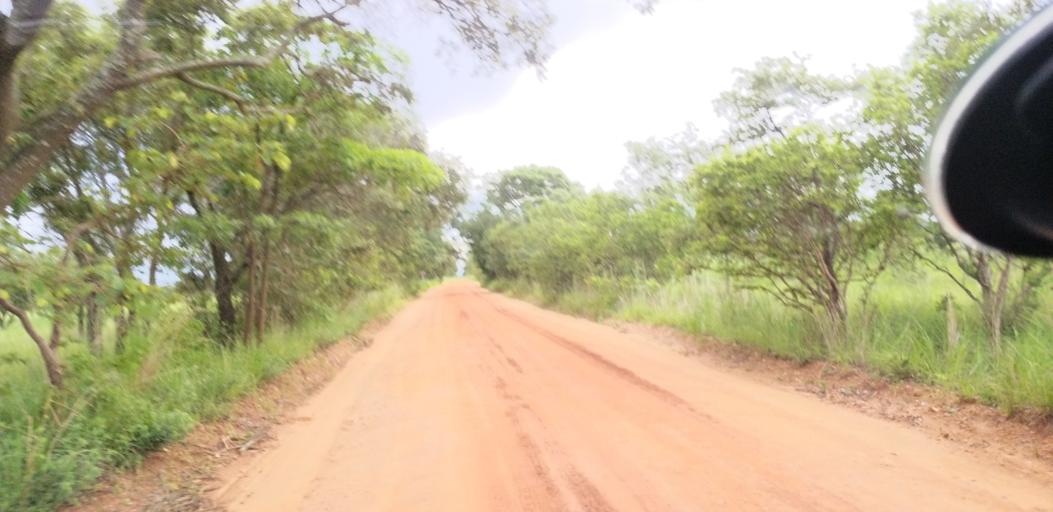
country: ZM
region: Lusaka
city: Chongwe
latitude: -15.1606
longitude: 28.4744
